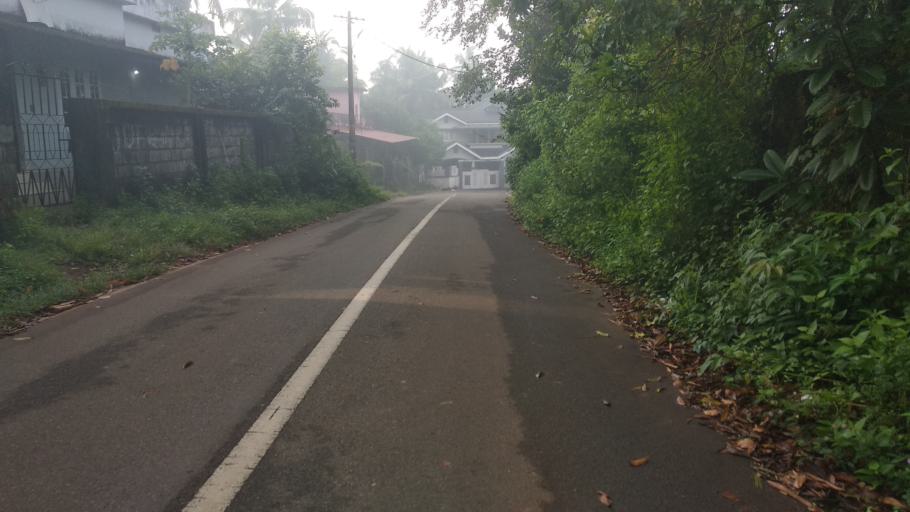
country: IN
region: Kerala
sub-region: Malappuram
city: Malappuram
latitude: 10.9916
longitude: 76.0472
